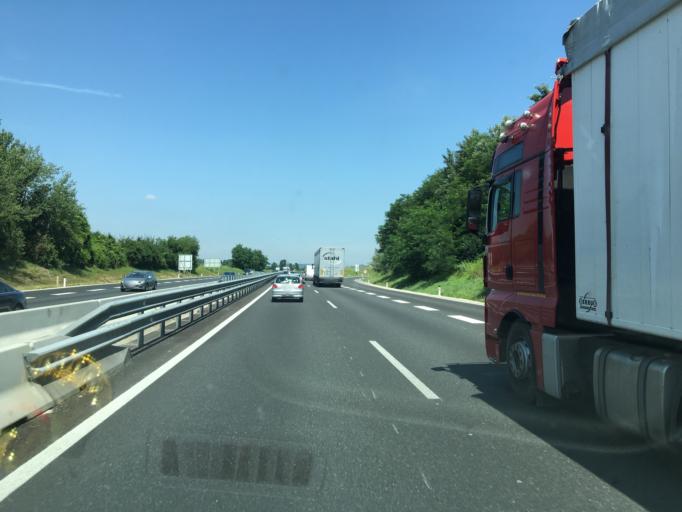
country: SI
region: Hoce-Slivnica
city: Rogoza
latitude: 46.5006
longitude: 15.6702
